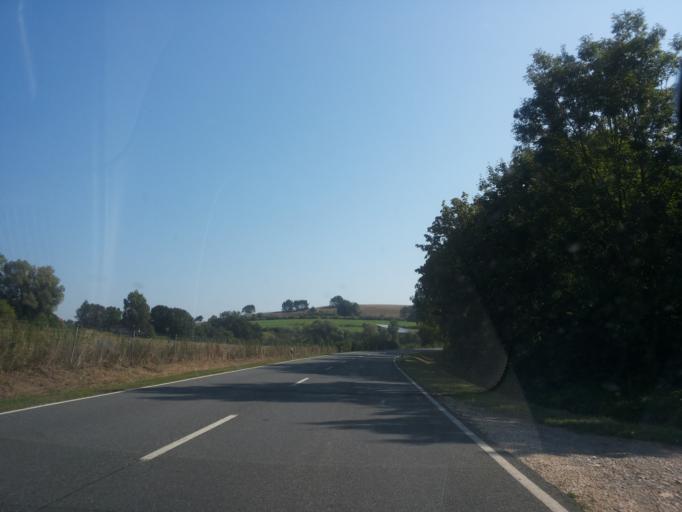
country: DE
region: Bavaria
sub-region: Lower Bavaria
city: Neustadt an der Donau
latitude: 48.8195
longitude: 11.7220
